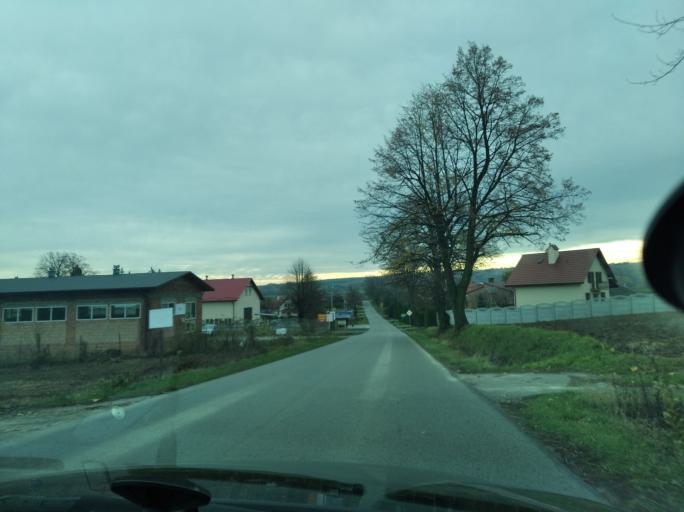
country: PL
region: Subcarpathian Voivodeship
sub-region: Powiat lancucki
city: Wysoka
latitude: 50.0203
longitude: 22.2607
